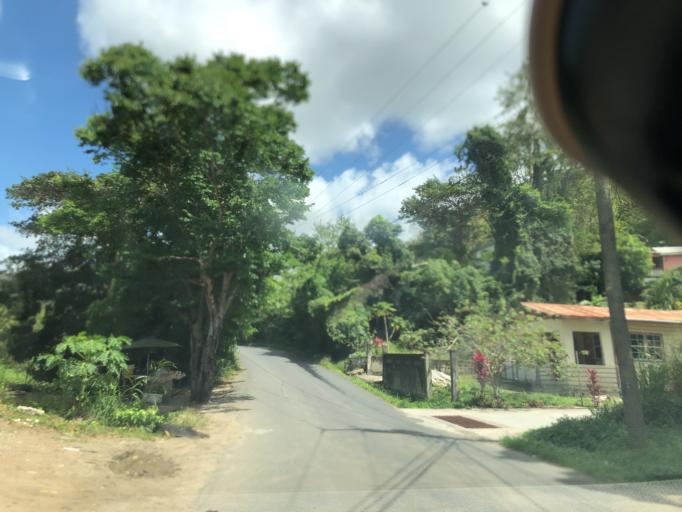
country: LC
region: Gros-Islet
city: Gros Islet
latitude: 14.0578
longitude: -60.9667
